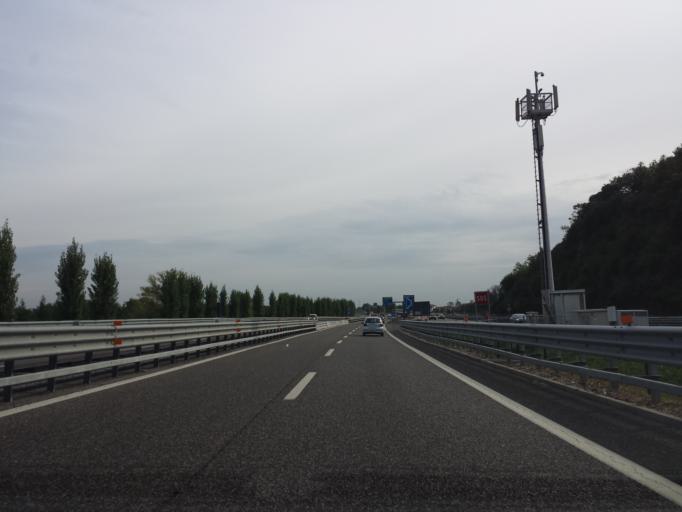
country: IT
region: Veneto
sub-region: Provincia di Vicenza
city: Arcugnano-Torri
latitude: 45.5160
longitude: 11.5538
